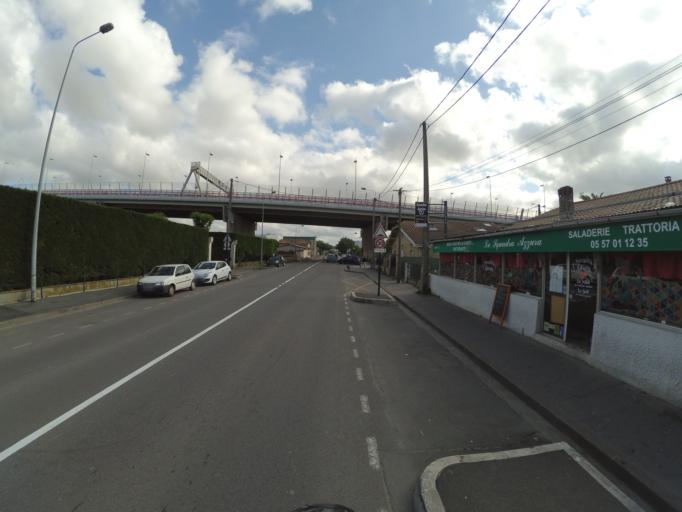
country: FR
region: Aquitaine
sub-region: Departement de la Gironde
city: Lormont
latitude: 44.8830
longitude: -0.5506
